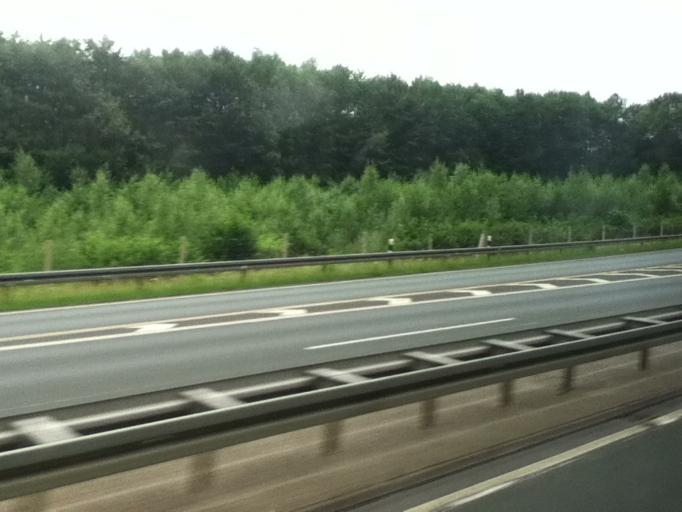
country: DE
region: North Rhine-Westphalia
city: Kreuztal
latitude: 50.9323
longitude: 8.0122
